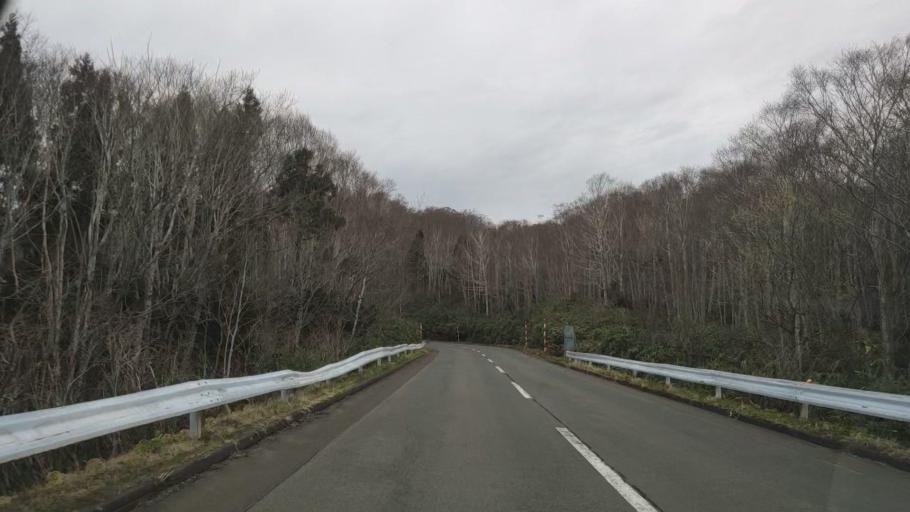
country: JP
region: Akita
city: Hanawa
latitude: 40.4159
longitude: 140.8464
